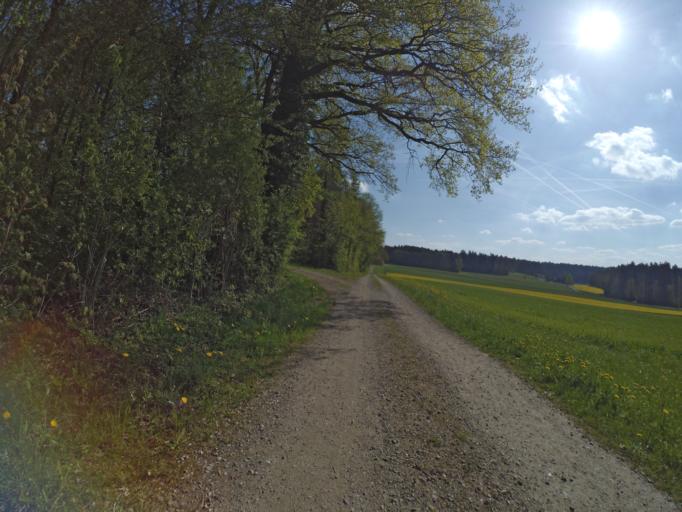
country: CH
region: Thurgau
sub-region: Frauenfeld District
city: Diessenhofen
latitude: 47.6574
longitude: 8.7522
